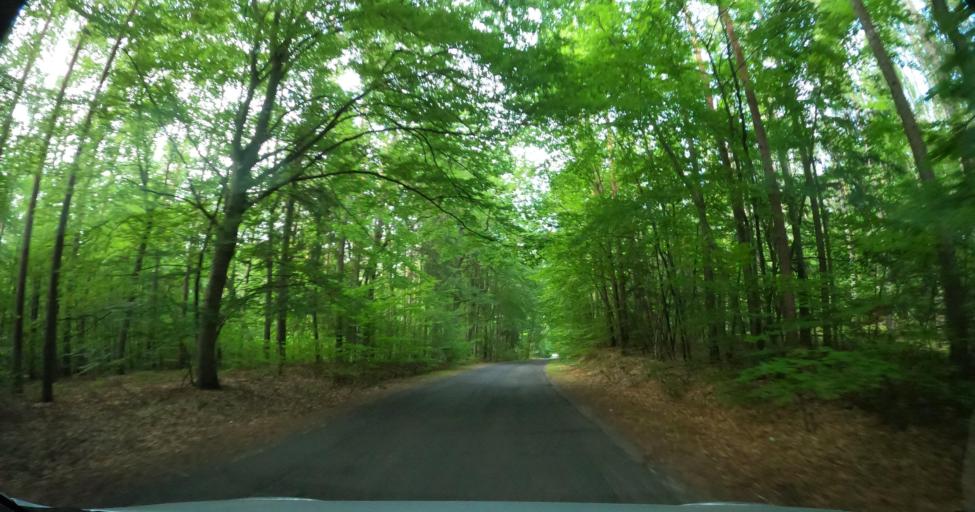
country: PL
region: West Pomeranian Voivodeship
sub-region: Powiat goleniowski
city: Goleniow
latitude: 53.5205
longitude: 14.8543
